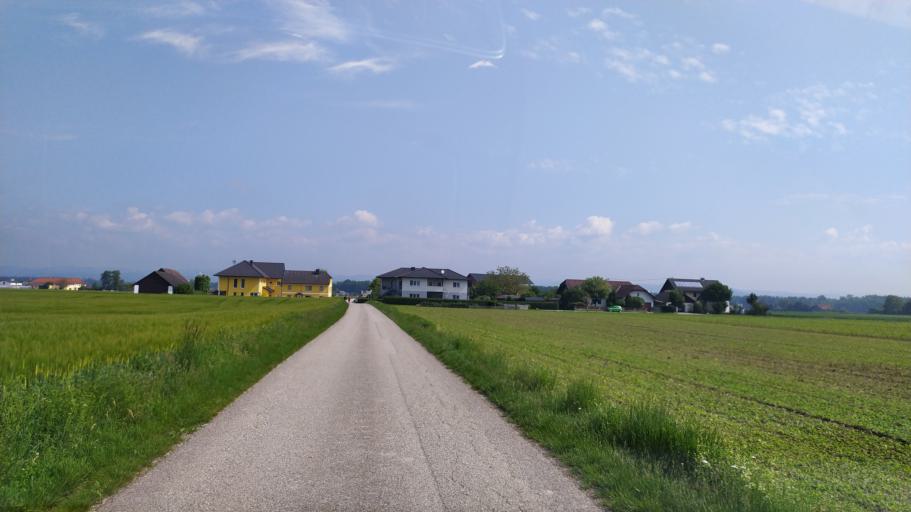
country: AT
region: Upper Austria
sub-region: Politischer Bezirk Perg
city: Perg
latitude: 48.1970
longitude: 14.6637
